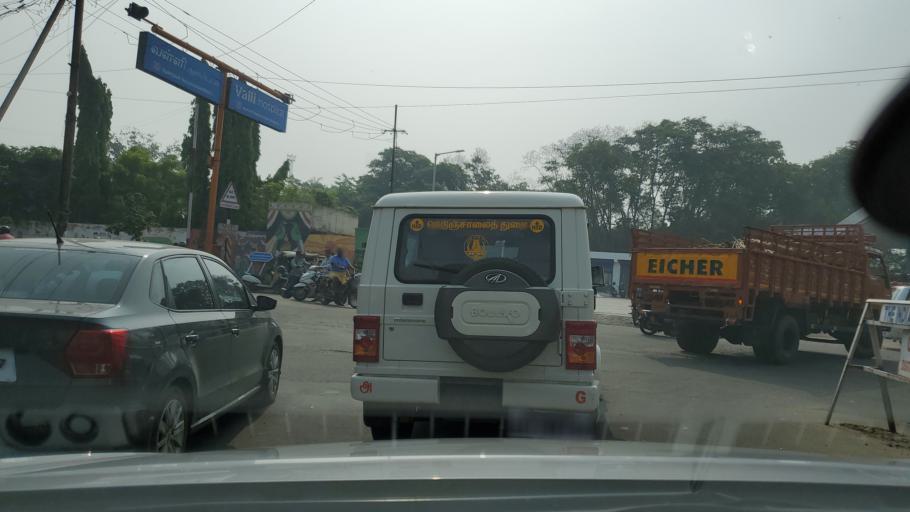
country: IN
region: Tamil Nadu
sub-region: Erode
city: Erode
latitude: 11.3292
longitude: 77.7239
